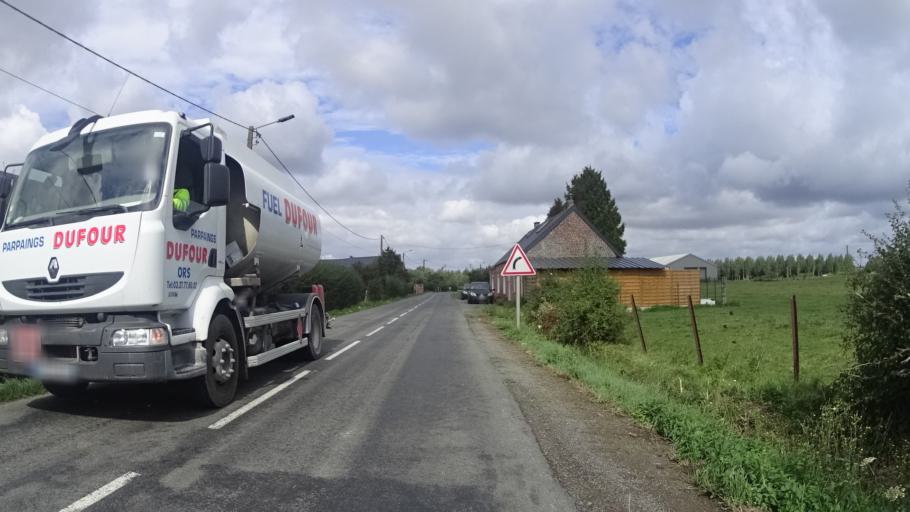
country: FR
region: Nord-Pas-de-Calais
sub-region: Departement du Nord
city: Landrecies
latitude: 50.0916
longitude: 3.6395
